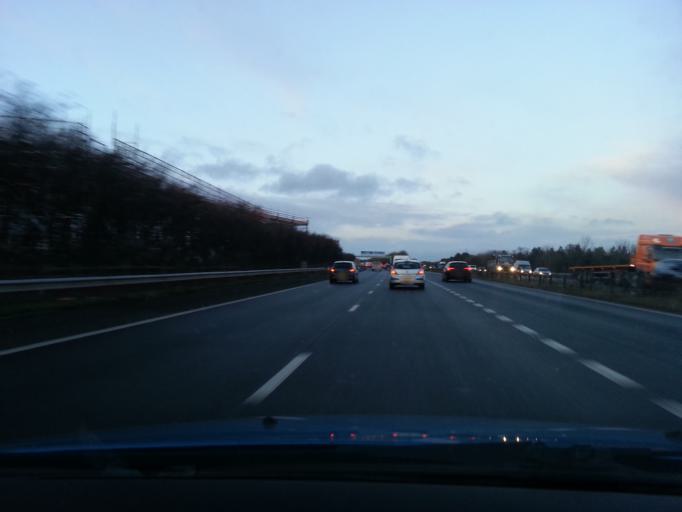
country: GB
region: England
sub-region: County Durham
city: Chester-le-Street
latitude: 54.8952
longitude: -1.5591
